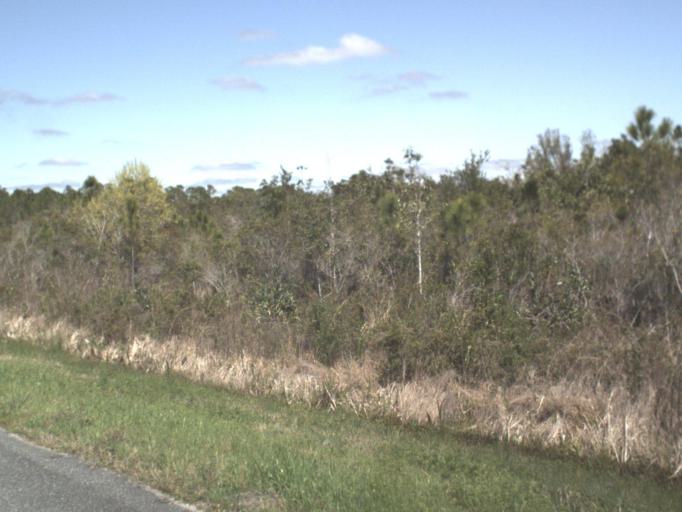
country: US
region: Florida
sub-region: Wakulla County
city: Crawfordville
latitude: 29.9934
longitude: -84.3957
